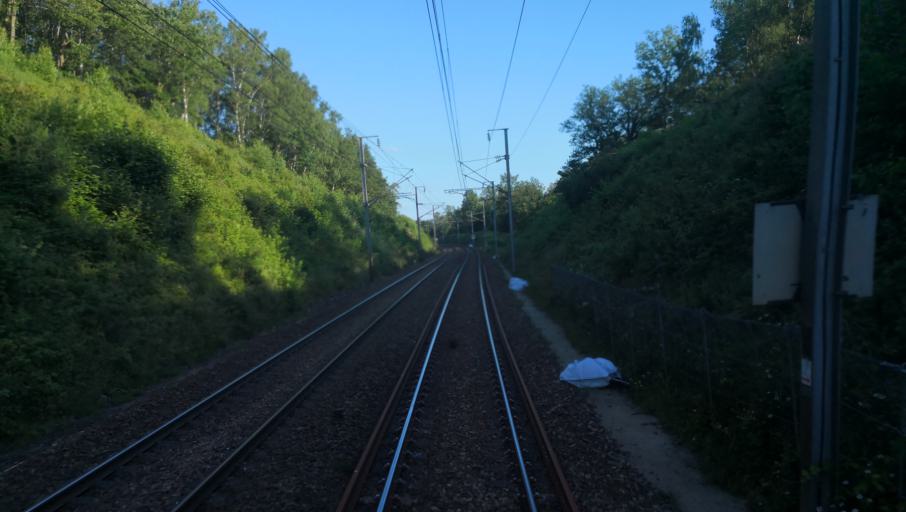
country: FR
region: Haute-Normandie
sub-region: Departement de l'Eure
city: Beaumont-le-Roger
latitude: 49.0273
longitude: 0.8221
